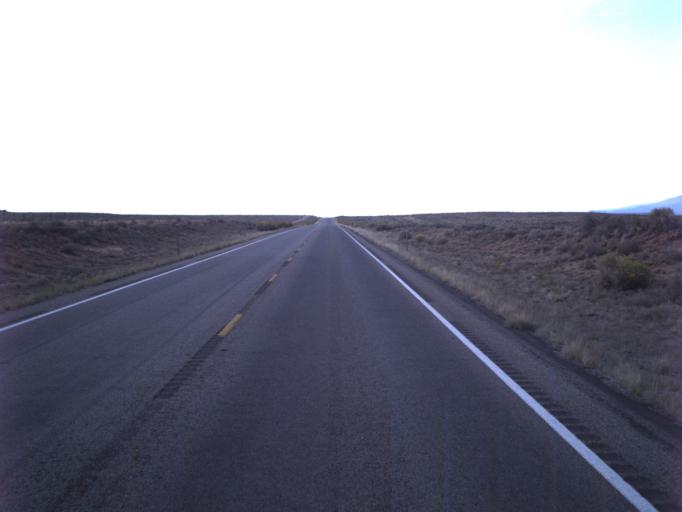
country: US
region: Utah
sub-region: San Juan County
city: Monticello
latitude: 38.1207
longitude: -109.3666
